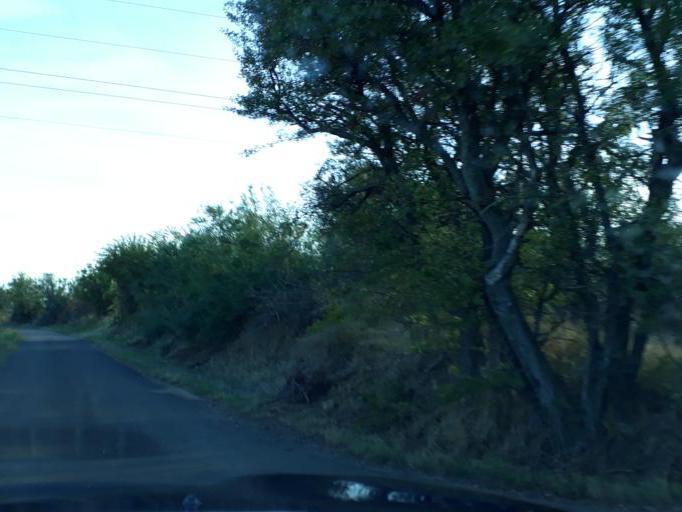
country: FR
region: Languedoc-Roussillon
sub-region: Departement de l'Herault
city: Florensac
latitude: 43.4154
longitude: 3.4737
